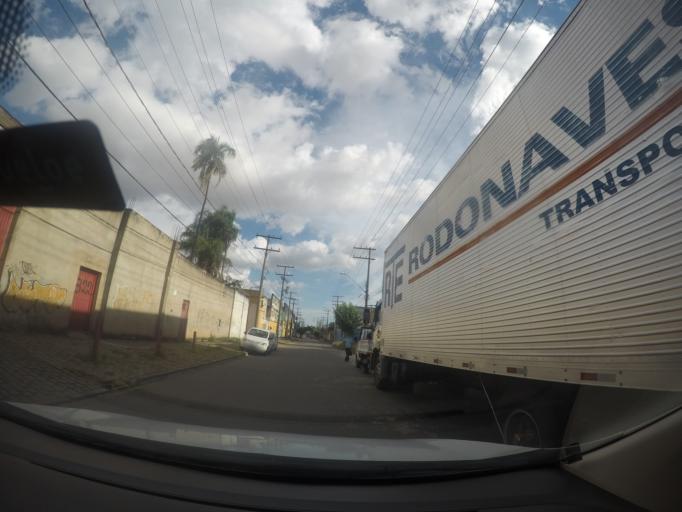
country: BR
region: Goias
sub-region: Goiania
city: Goiania
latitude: -16.6700
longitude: -49.3003
